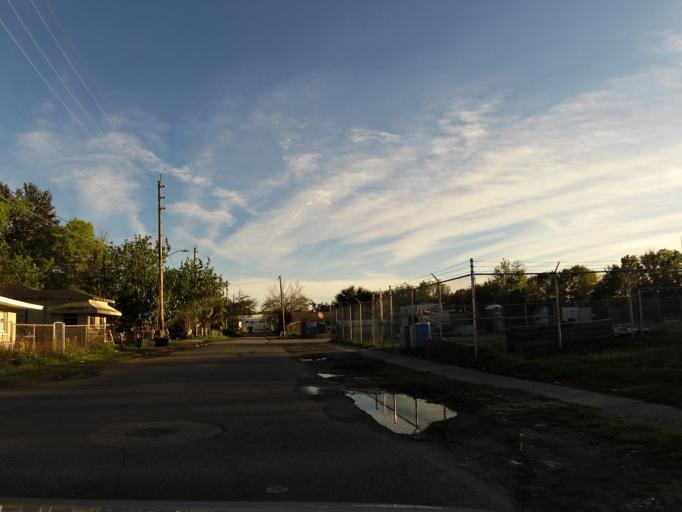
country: US
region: Florida
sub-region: Duval County
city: Jacksonville
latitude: 30.3360
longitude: -81.6987
